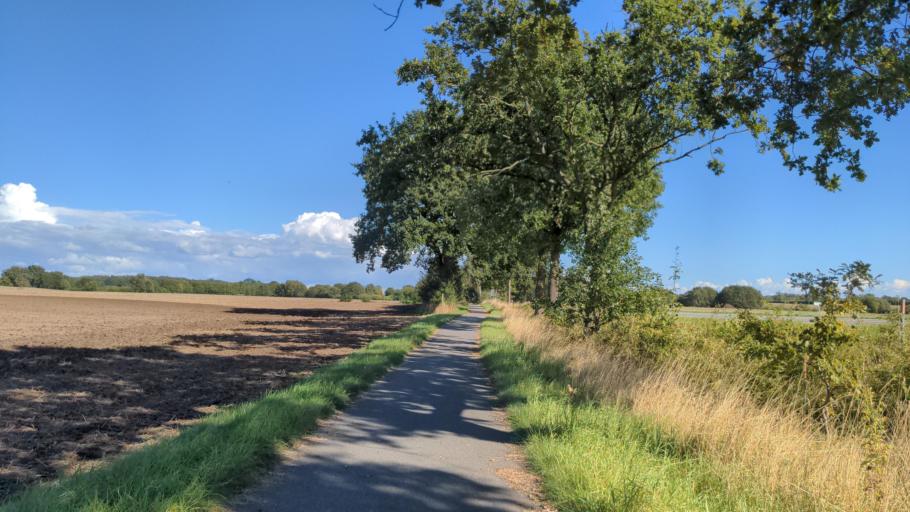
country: DE
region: Schleswig-Holstein
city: Beschendorf
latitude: 54.1611
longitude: 10.8694
